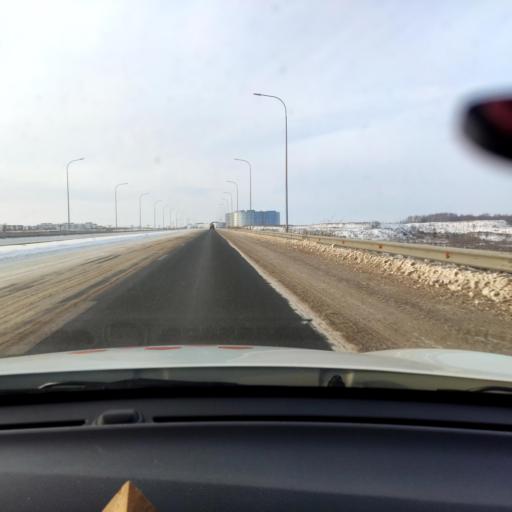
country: RU
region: Tatarstan
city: Sviyazhsk
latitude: 55.7469
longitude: 48.7657
